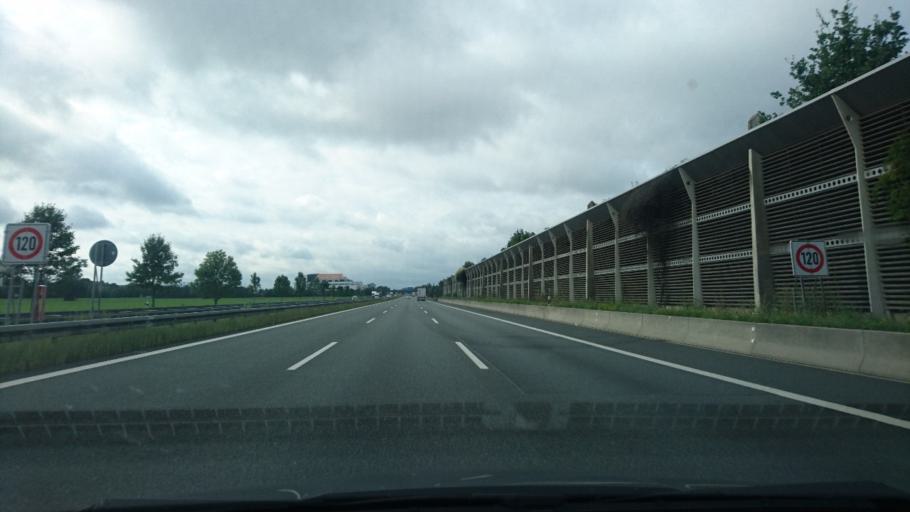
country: DE
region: Bavaria
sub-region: Upper Franconia
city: Bindlach
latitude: 49.9761
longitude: 11.6064
